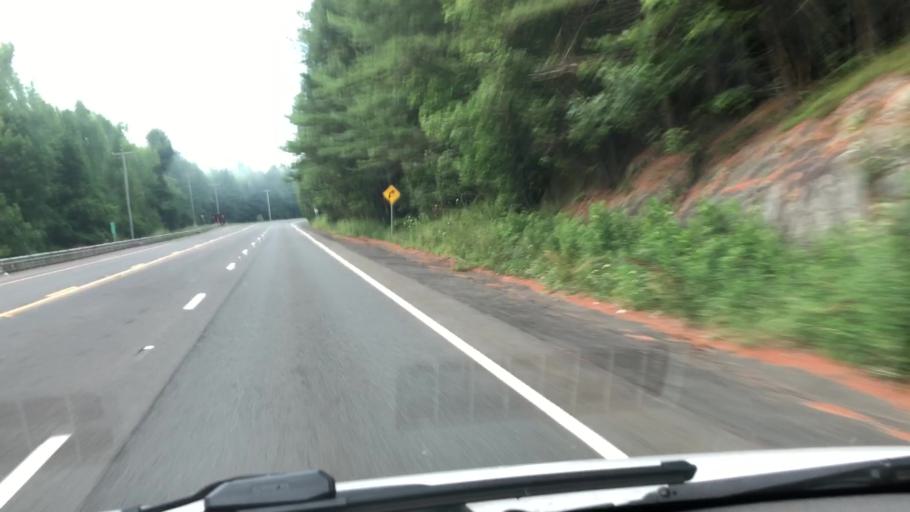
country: US
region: Massachusetts
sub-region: Berkshire County
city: Hinsdale
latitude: 42.4863
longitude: -72.9797
